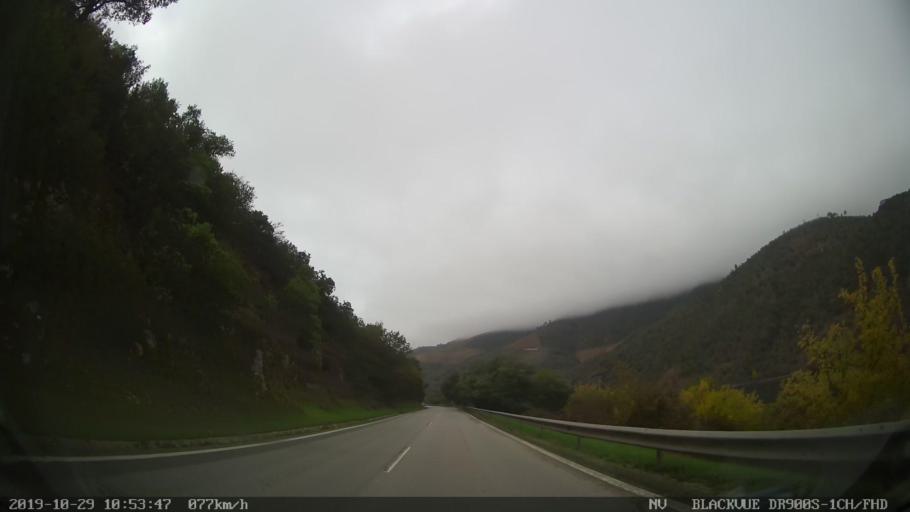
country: PT
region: Viseu
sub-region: Armamar
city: Armamar
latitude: 41.1616
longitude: -7.6590
